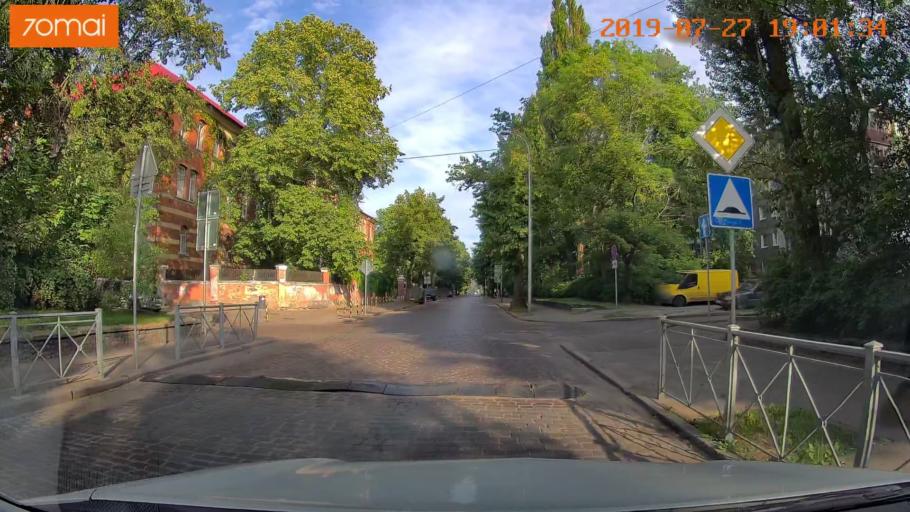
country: RU
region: Kaliningrad
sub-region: Gorod Kaliningrad
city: Kaliningrad
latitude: 54.7261
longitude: 20.4894
